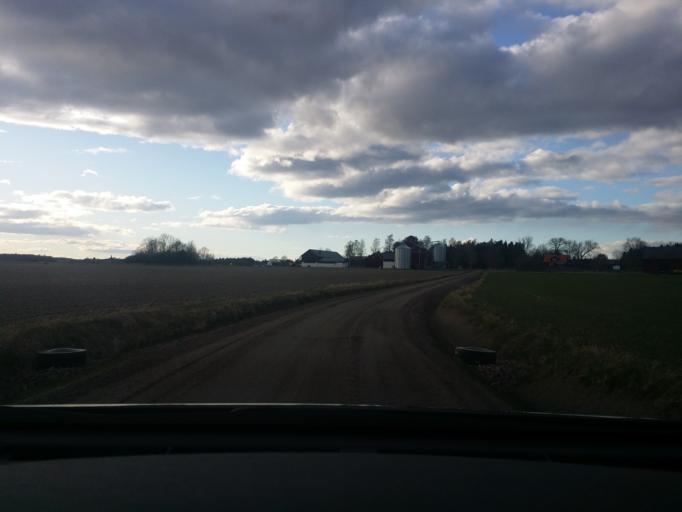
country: SE
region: Vaestmanland
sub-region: Vasteras
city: Vasteras
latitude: 59.5532
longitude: 16.4521
